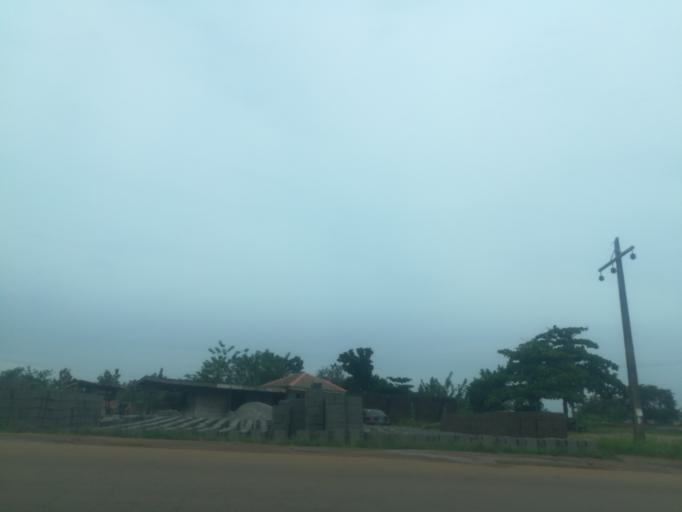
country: NG
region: Oyo
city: Egbeda
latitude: 7.3831
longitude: 4.0148
